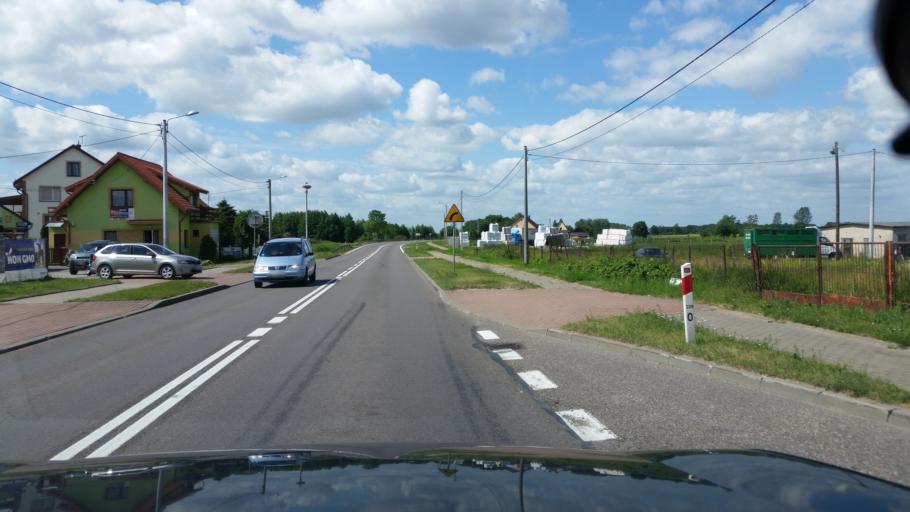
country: PL
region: Podlasie
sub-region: Powiat grajewski
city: Rajgrod
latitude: 53.6835
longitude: 22.6182
